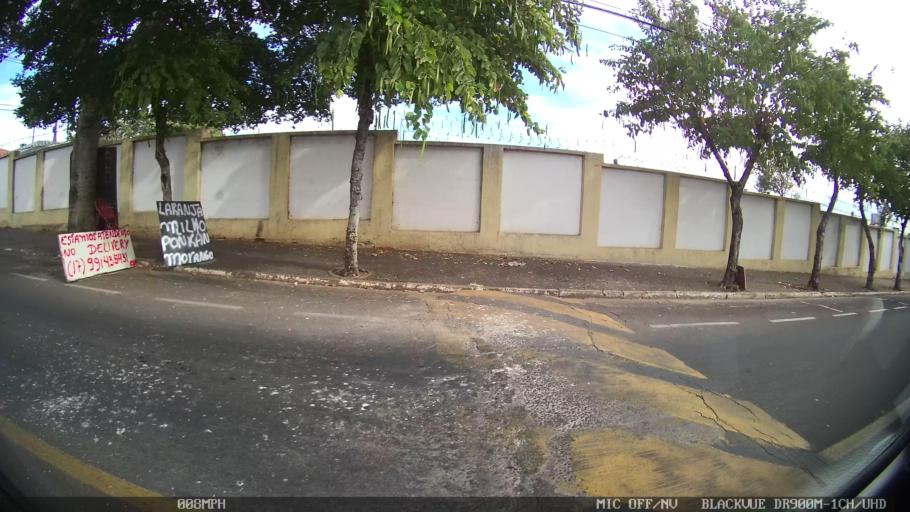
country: BR
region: Sao Paulo
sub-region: Catanduva
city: Catanduva
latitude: -21.1379
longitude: -48.9803
